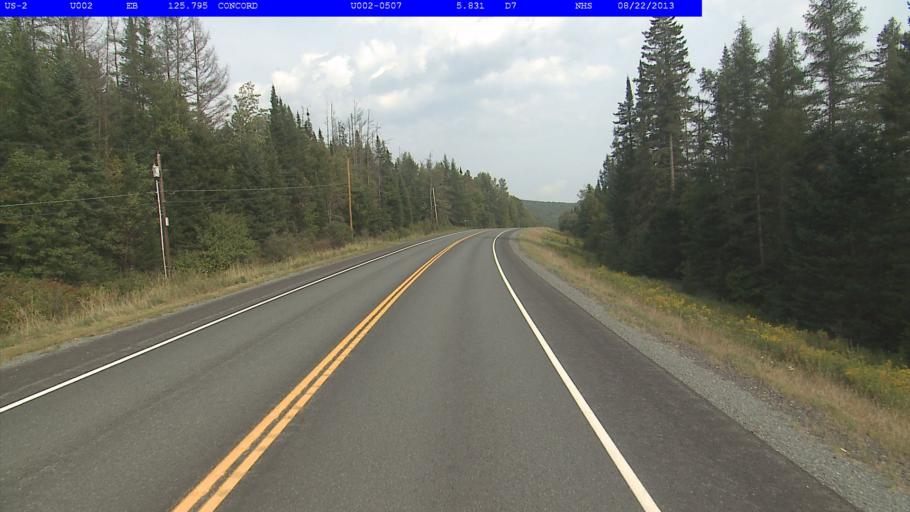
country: US
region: Vermont
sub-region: Caledonia County
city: Lyndonville
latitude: 44.4692
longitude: -71.8493
